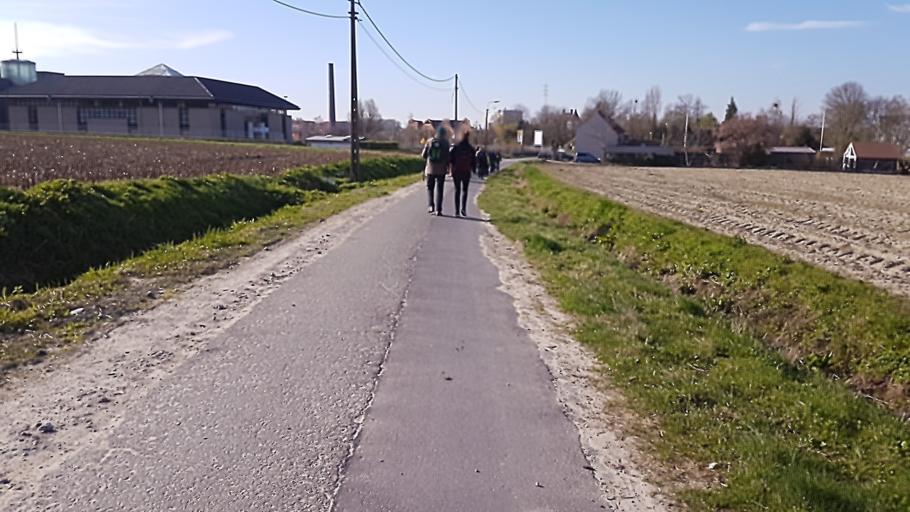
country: BE
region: Flanders
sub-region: Provincie West-Vlaanderen
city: Harelbeke
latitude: 50.8238
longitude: 3.3072
